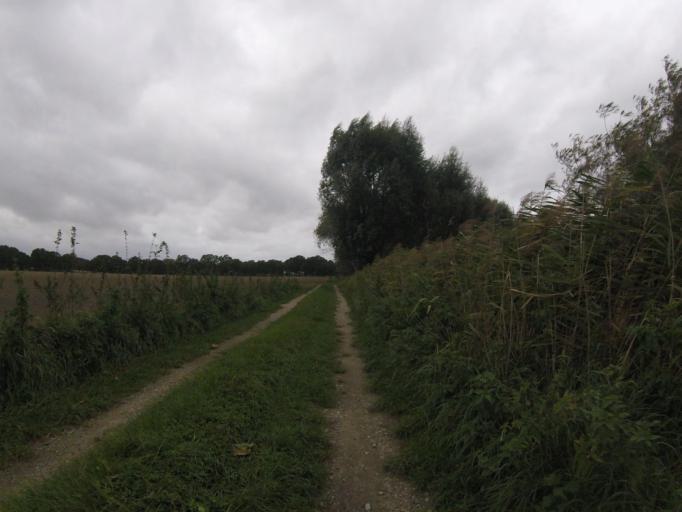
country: DE
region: Brandenburg
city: Mittenwalde
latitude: 52.2903
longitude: 13.5740
